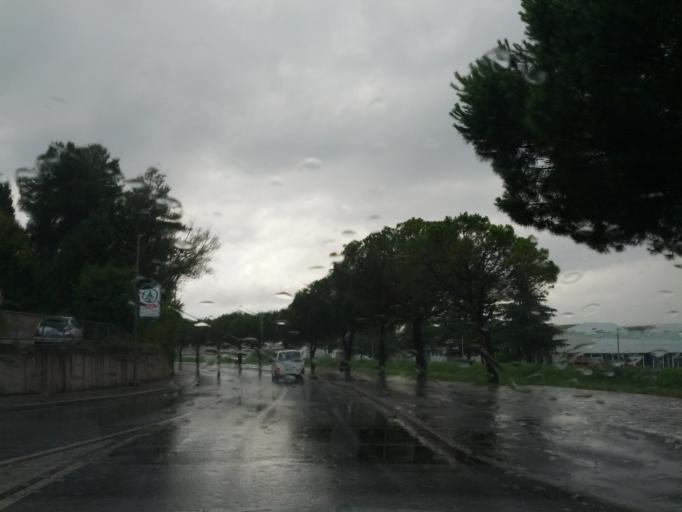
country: SI
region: Koper-Capodistria
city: Koper
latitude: 45.5386
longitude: 13.7260
